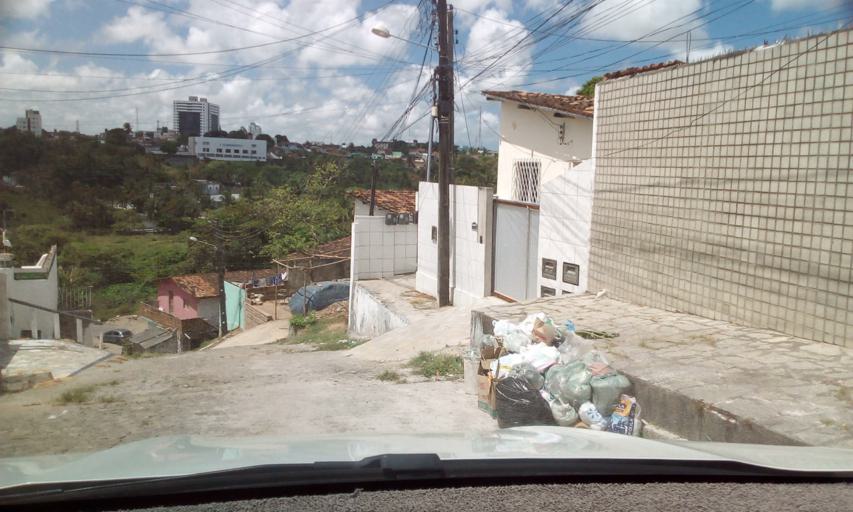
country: BR
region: Paraiba
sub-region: Joao Pessoa
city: Joao Pessoa
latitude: -7.1431
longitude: -34.8767
